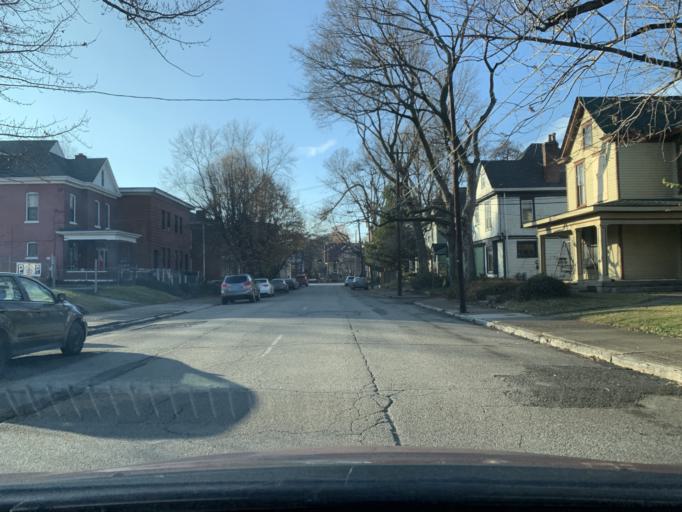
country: US
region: Kentucky
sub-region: Jefferson County
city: Louisville
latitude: 38.2293
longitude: -85.7531
